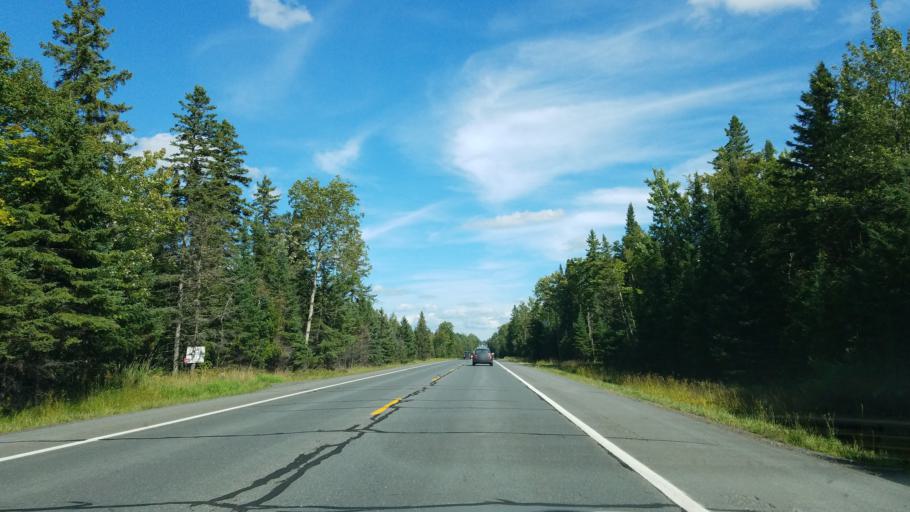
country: US
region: Michigan
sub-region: Baraga County
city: L'Anse
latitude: 46.5788
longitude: -88.4219
